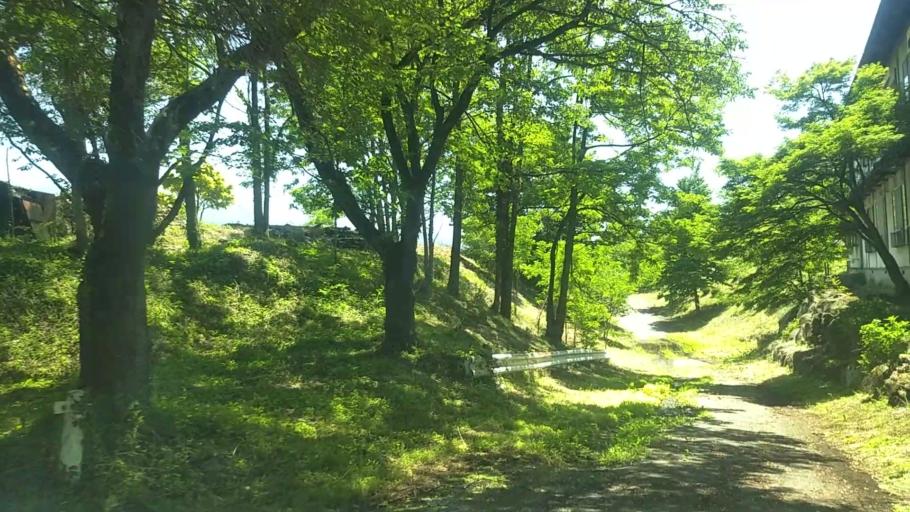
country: JP
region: Yamanashi
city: Nirasaki
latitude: 35.7803
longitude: 138.4161
